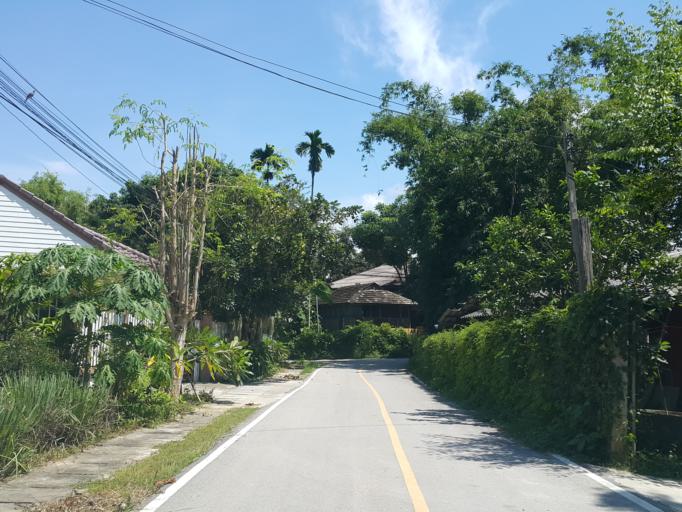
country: TH
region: Chiang Mai
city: San Sai
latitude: 18.8129
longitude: 99.0968
